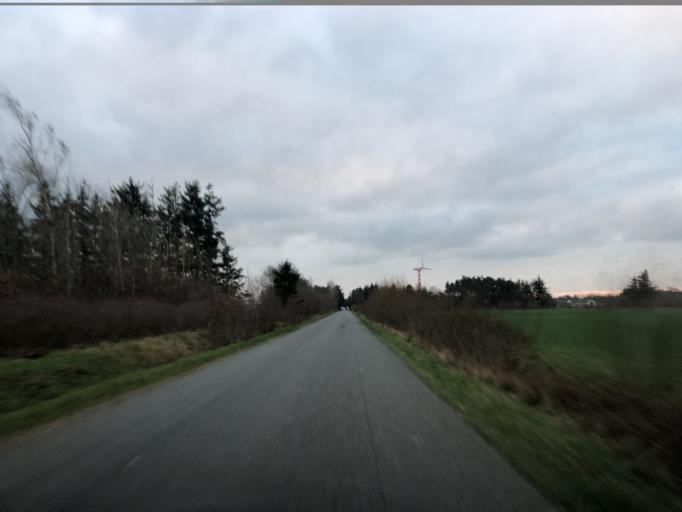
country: DK
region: Central Jutland
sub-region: Holstebro Kommune
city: Ulfborg
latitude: 56.2624
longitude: 8.2851
